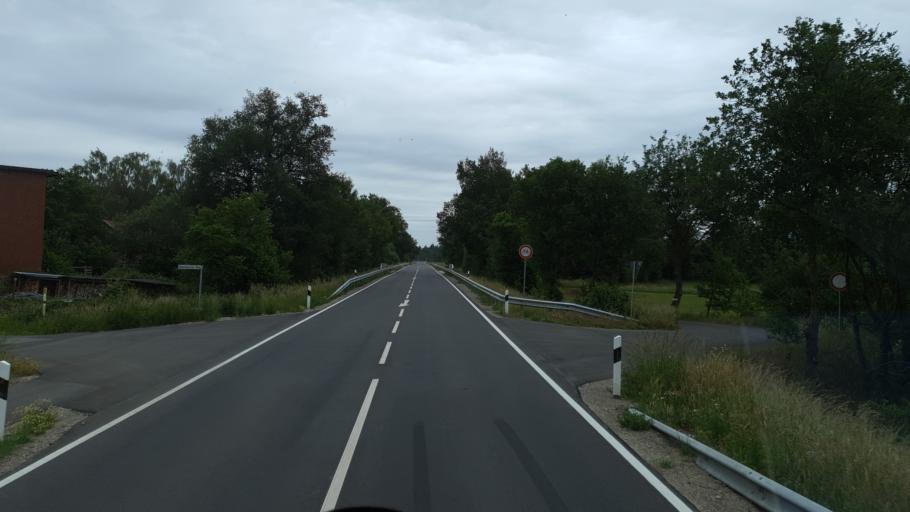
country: NL
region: Overijssel
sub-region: Gemeente Losser
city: Losser
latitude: 52.2698
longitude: 7.0543
